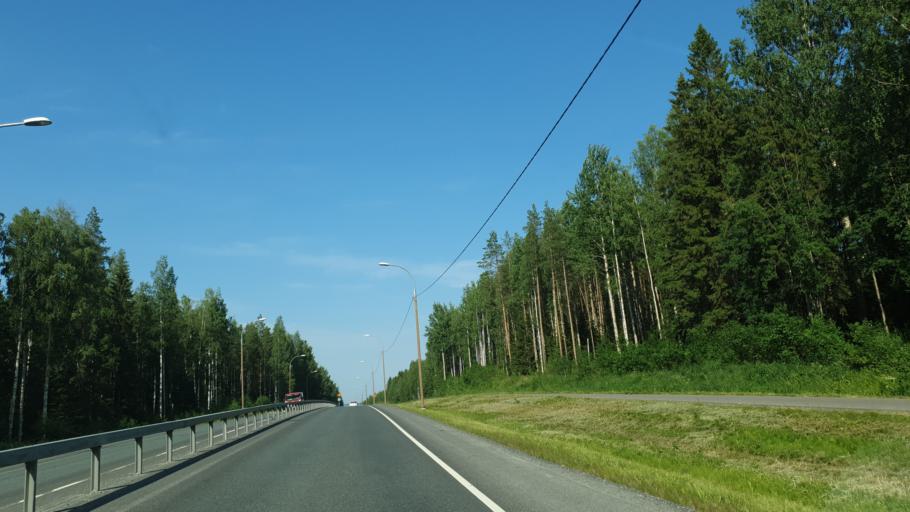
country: FI
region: Northern Savo
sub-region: Kuopio
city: Siilinjaervi
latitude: 63.1025
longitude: 27.7421
